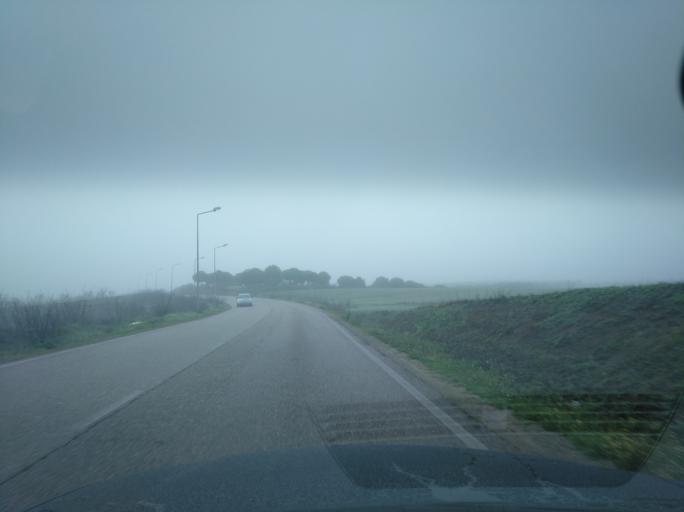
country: PT
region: Portalegre
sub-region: Campo Maior
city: Campo Maior
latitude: 39.0259
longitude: -7.0709
